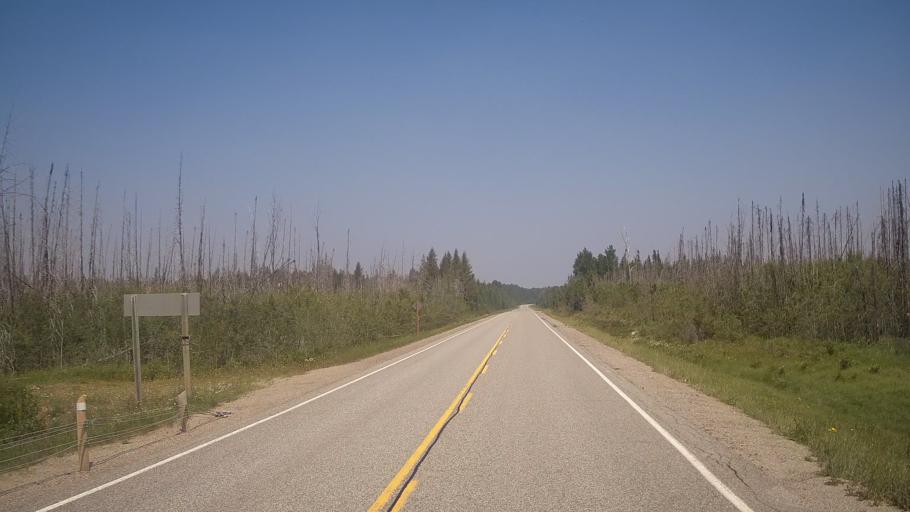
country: CA
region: Ontario
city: Timmins
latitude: 48.2215
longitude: -81.5728
